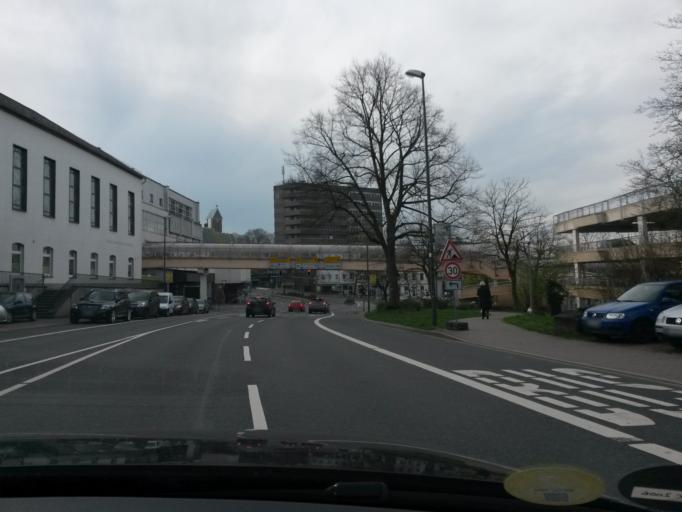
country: DE
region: North Rhine-Westphalia
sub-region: Regierungsbezirk Arnsberg
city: Luedenscheid
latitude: 51.2172
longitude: 7.6260
